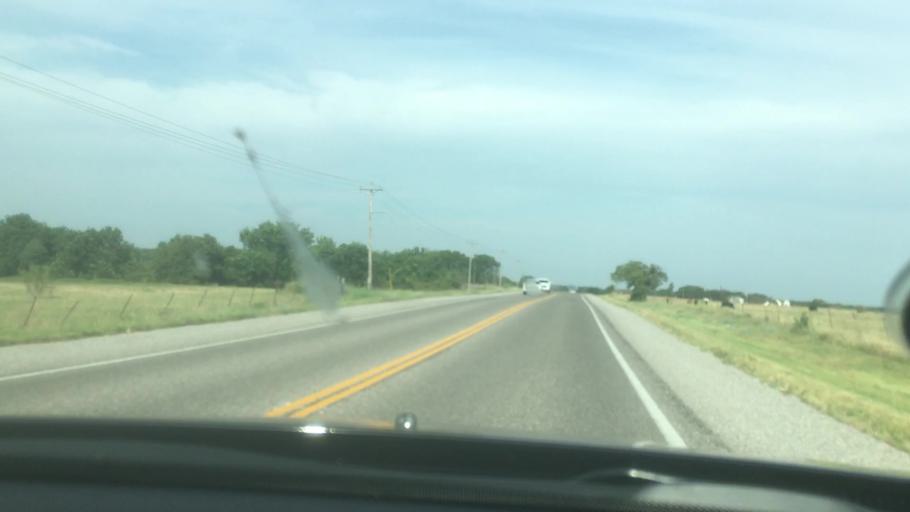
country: US
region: Oklahoma
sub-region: Garvin County
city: Pauls Valley
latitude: 34.7966
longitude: -97.0971
